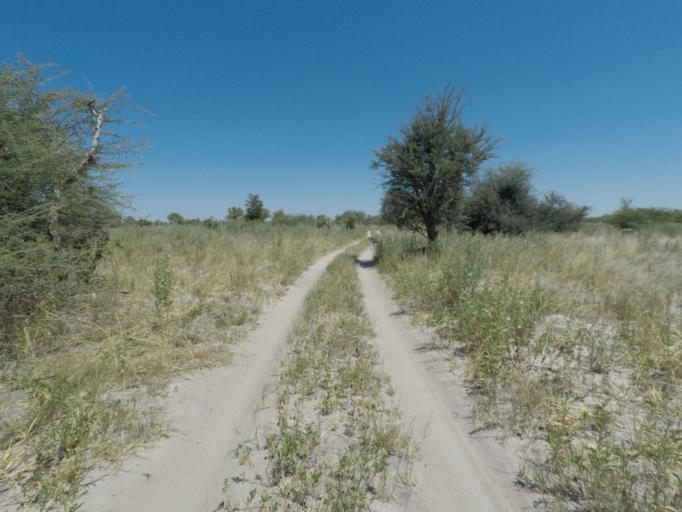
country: BW
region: North West
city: Maun
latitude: -19.4427
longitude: 23.5598
